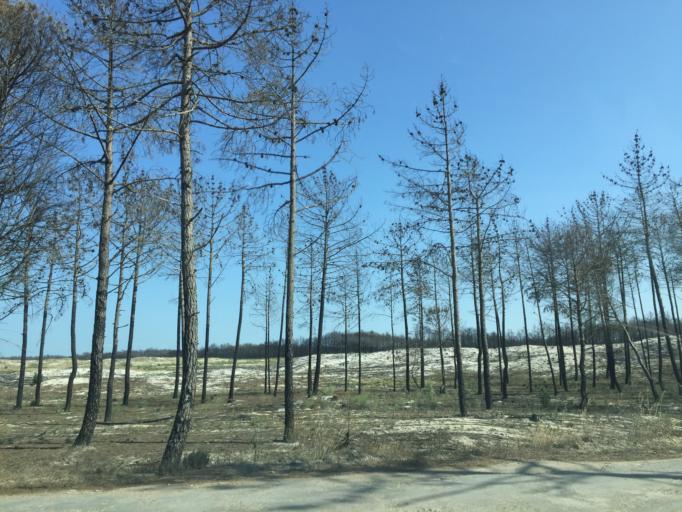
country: PT
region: Coimbra
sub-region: Figueira da Foz
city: Alhadas
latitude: 40.2570
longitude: -8.8367
